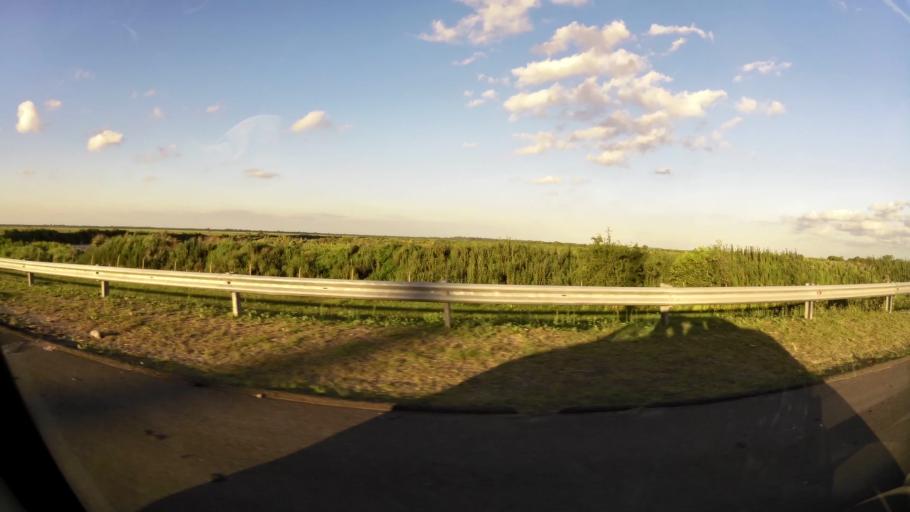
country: AR
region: Buenos Aires
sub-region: Partido de Quilmes
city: Quilmes
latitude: -34.8003
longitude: -58.1271
